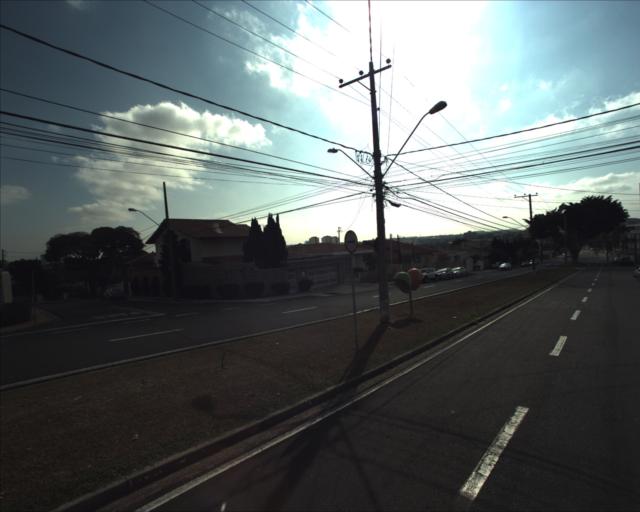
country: BR
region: Sao Paulo
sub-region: Sorocaba
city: Sorocaba
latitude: -23.4862
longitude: -47.4456
